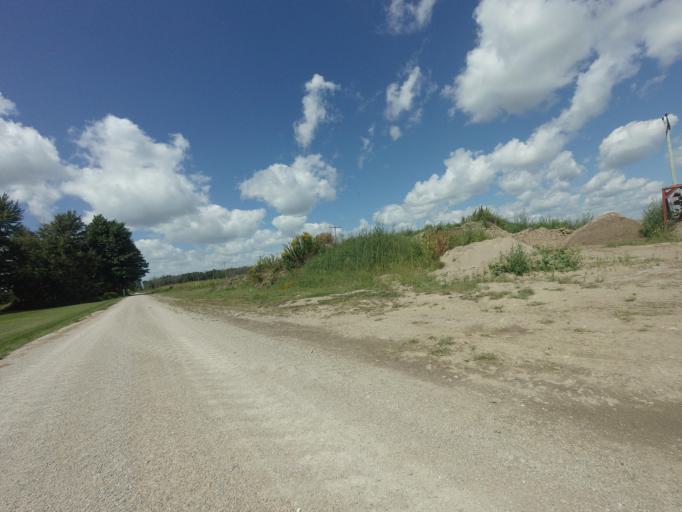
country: CA
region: Ontario
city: North Perth
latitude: 43.5909
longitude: -81.0834
